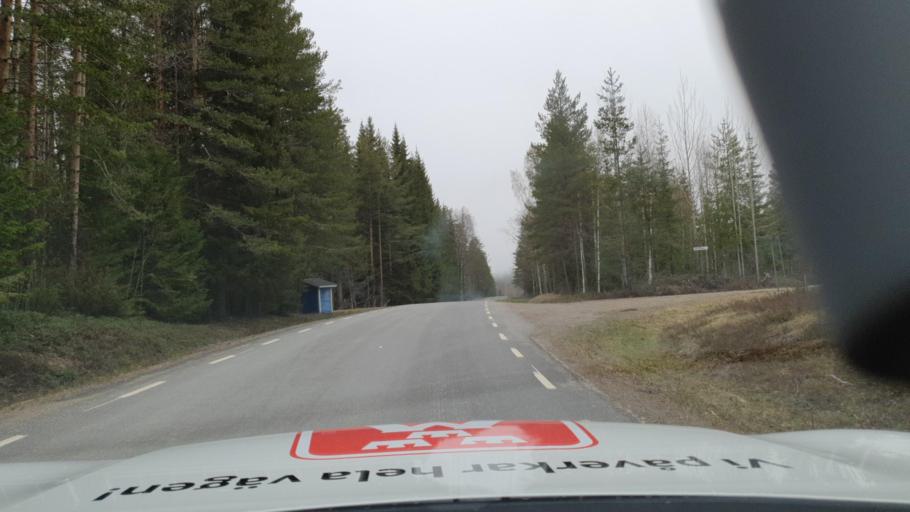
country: SE
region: Vaesterbotten
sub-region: Nordmalings Kommun
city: Nordmaling
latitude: 63.7318
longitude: 19.5027
